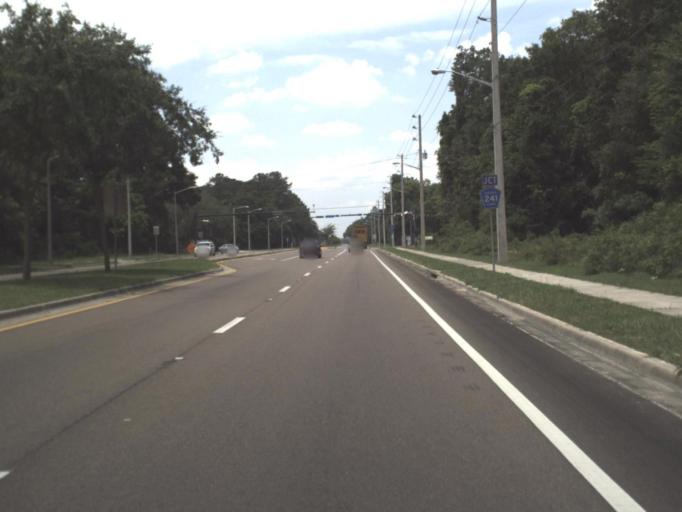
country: US
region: Florida
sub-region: Alachua County
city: Newberry
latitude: 29.6542
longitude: -82.5216
